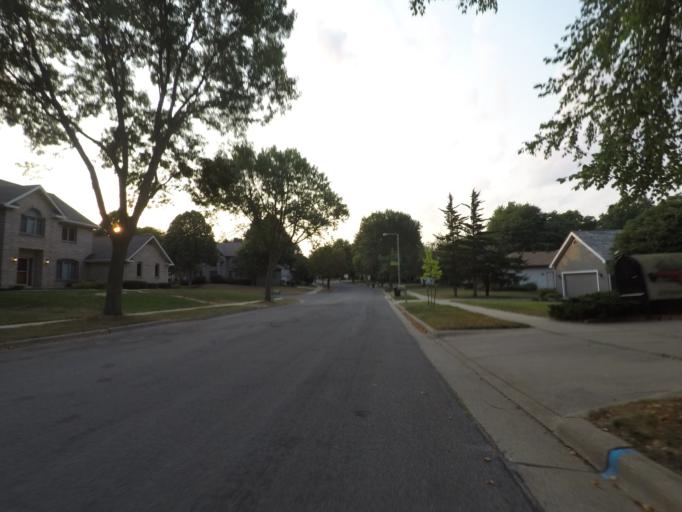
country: US
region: Wisconsin
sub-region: Dane County
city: Middleton
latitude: 43.0705
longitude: -89.5164
